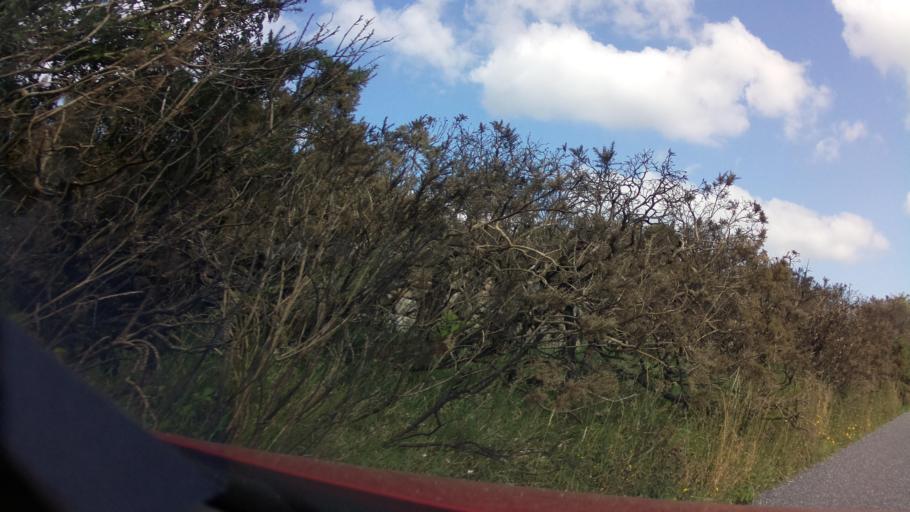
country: GB
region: England
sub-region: Devon
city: South Brent
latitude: 50.5547
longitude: -3.9109
